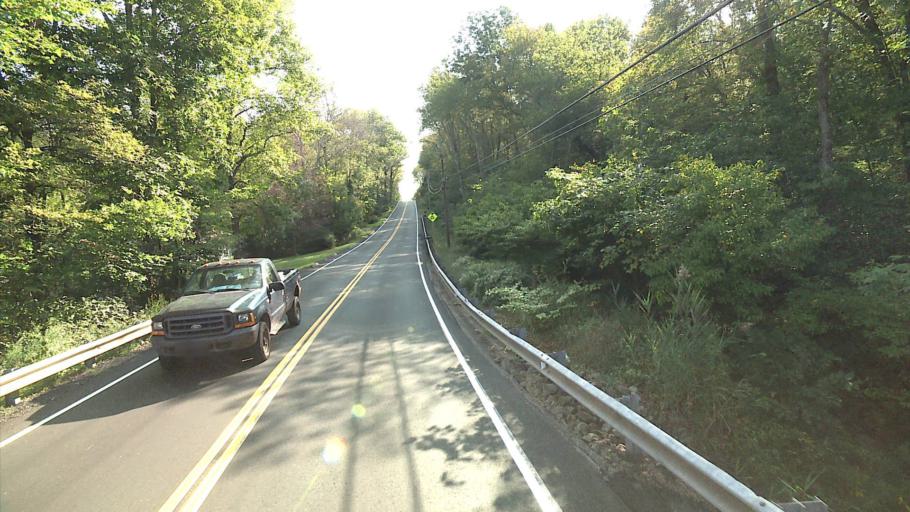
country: US
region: Connecticut
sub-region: Tolland County
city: Hebron
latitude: 41.7222
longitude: -72.4153
